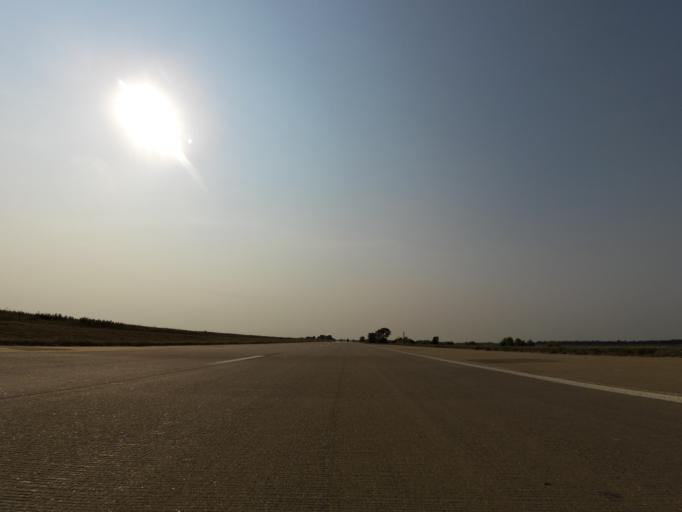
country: US
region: Kansas
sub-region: Sedgwick County
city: Colwich
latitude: 37.8423
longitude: -97.5777
